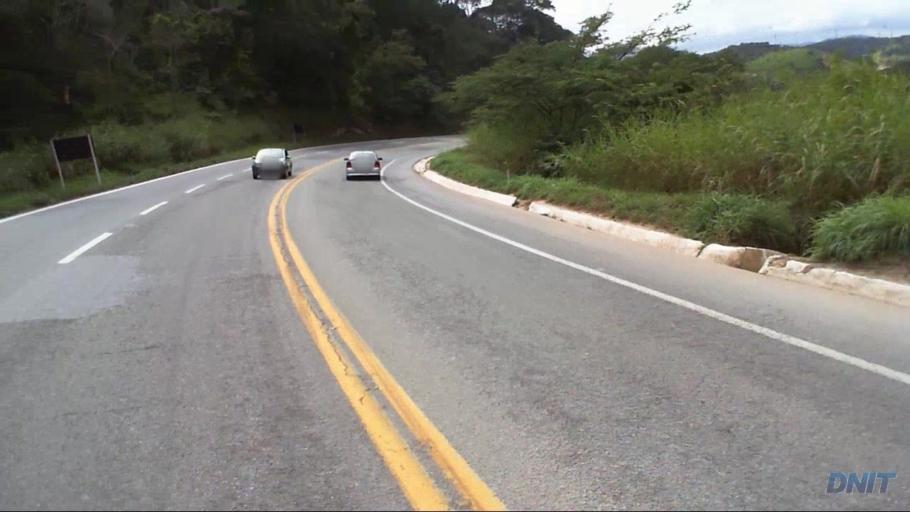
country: BR
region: Minas Gerais
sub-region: Caete
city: Caete
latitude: -19.7550
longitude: -43.6311
